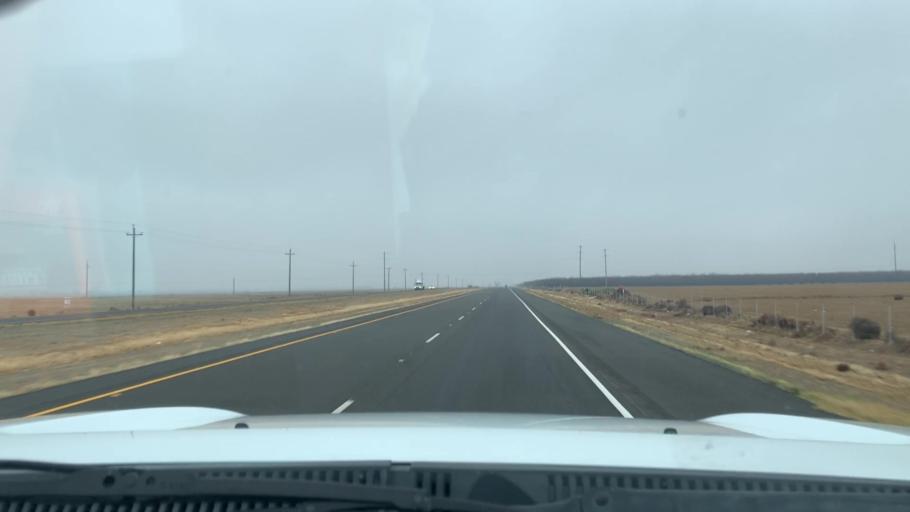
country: US
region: California
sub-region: Kern County
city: Lost Hills
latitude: 35.6157
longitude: -119.7651
